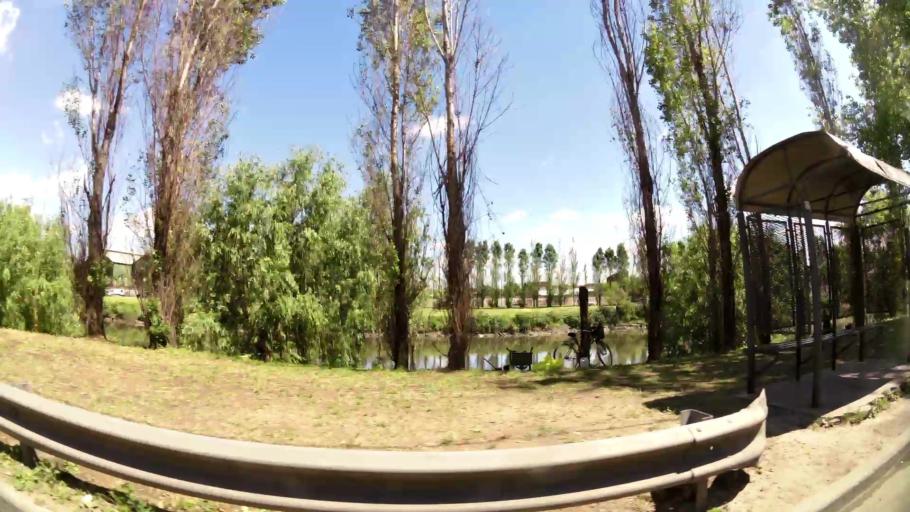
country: AR
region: Buenos Aires F.D.
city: Villa Lugano
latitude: -34.6656
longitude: -58.4269
